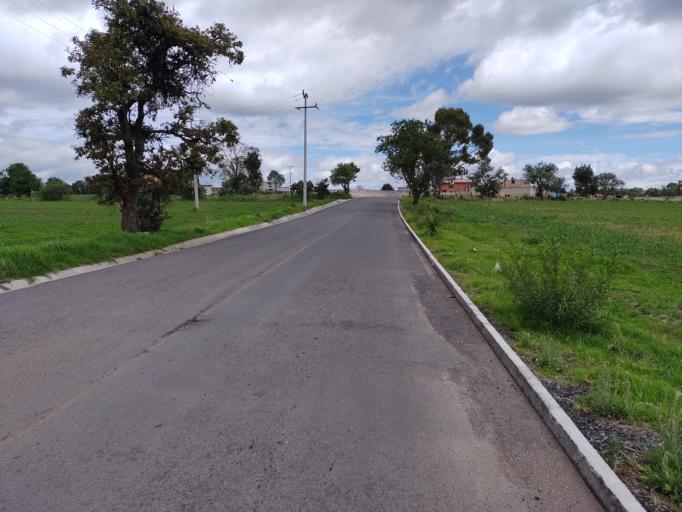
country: MX
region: Mexico
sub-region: Aculco
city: Gunyo Poniente (San Jose Gunyo)
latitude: 20.1169
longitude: -99.8766
